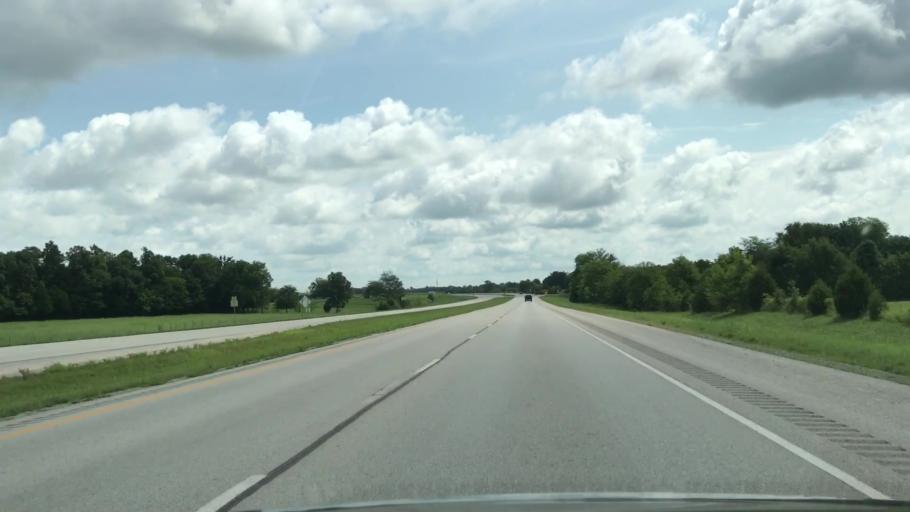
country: US
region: Kentucky
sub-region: Logan County
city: Auburn
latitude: 36.8919
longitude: -86.6160
